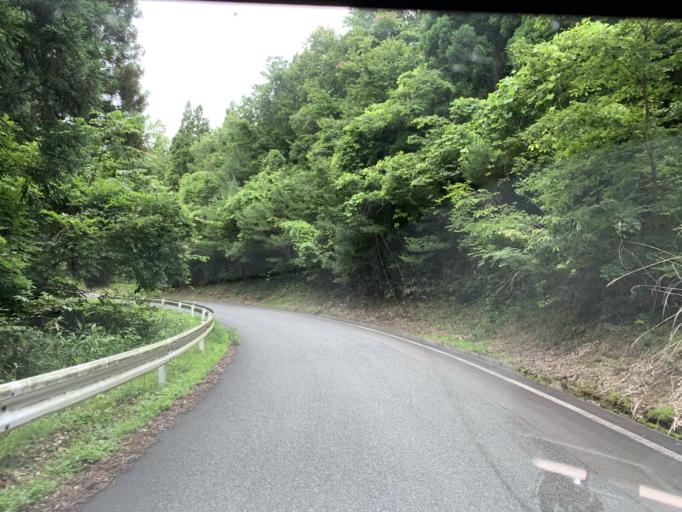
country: JP
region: Iwate
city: Ichinoseki
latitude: 38.9037
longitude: 140.9991
